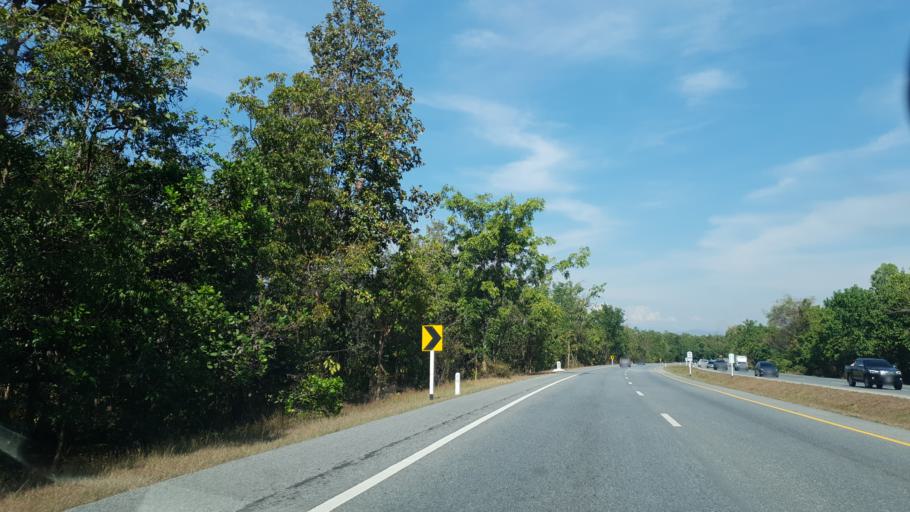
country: TH
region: Uttaradit
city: Thong Saen Khan
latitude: 17.4253
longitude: 100.2257
